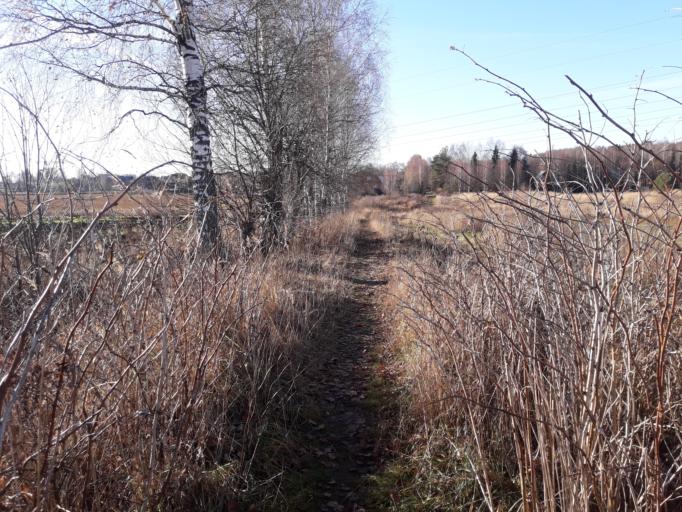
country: RU
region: Moskovskaya
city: Ashukino
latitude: 56.1591
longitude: 37.9633
